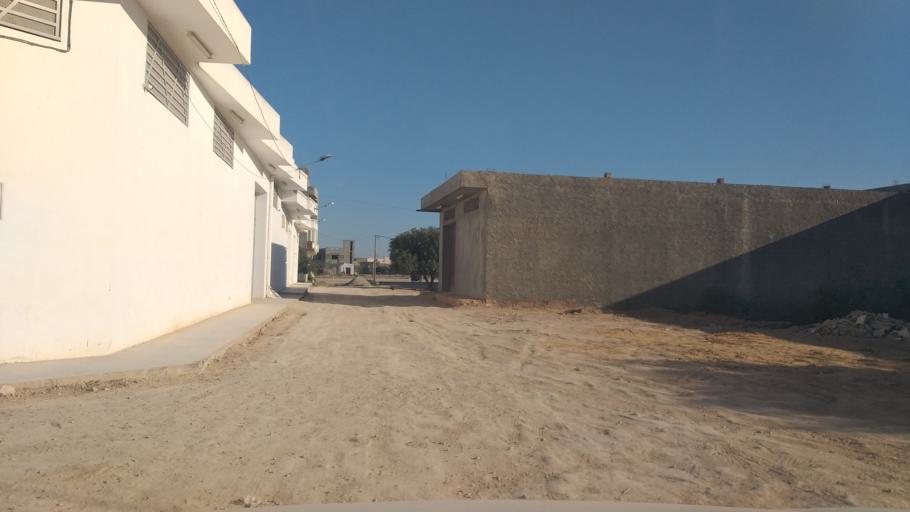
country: TN
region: Al Mahdiyah
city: El Jem
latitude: 35.2937
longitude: 10.6942
